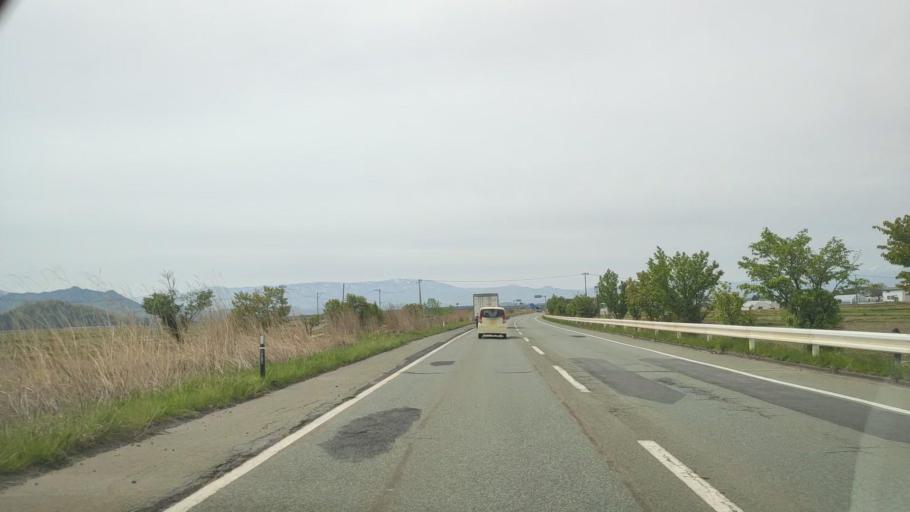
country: JP
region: Yamagata
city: Takahata
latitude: 38.0371
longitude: 140.1733
